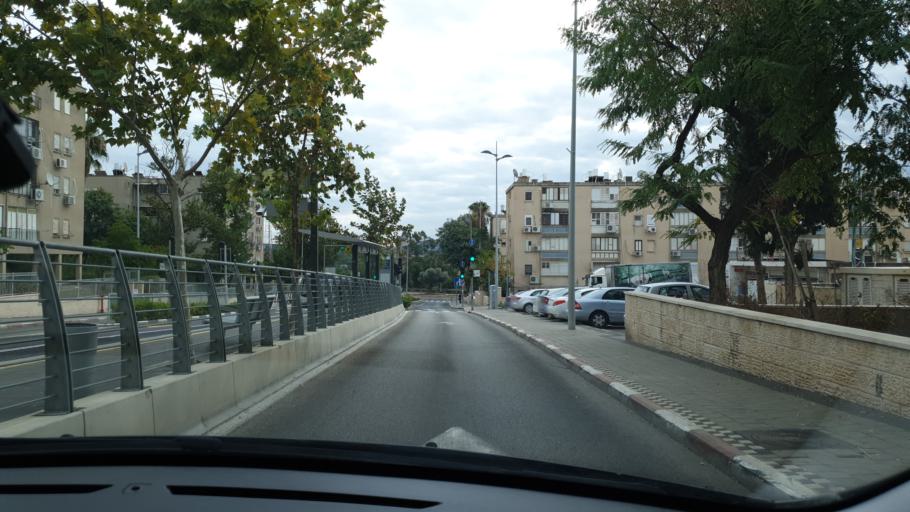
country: IL
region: Haifa
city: Qiryat Ata
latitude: 32.8084
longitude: 35.1165
